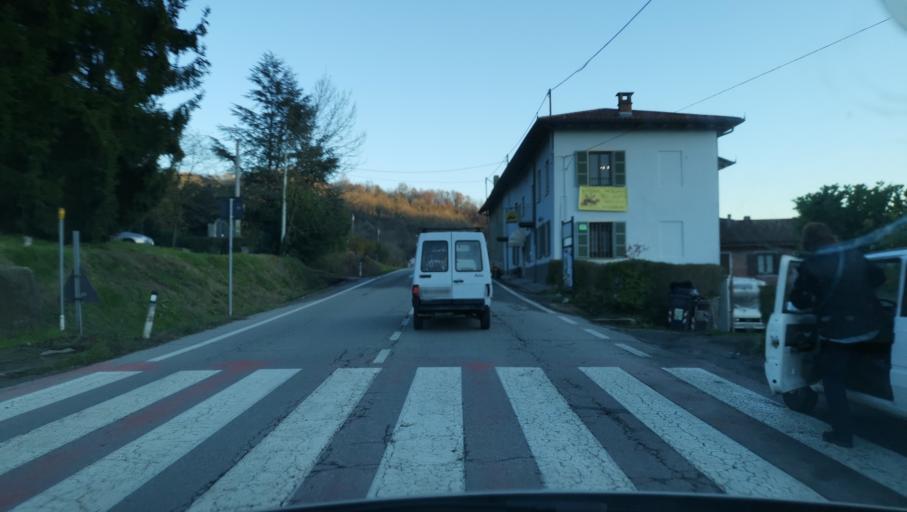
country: IT
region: Piedmont
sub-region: Provincia di Torino
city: San Raffaele Cimena
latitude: 45.1254
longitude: 7.8539
